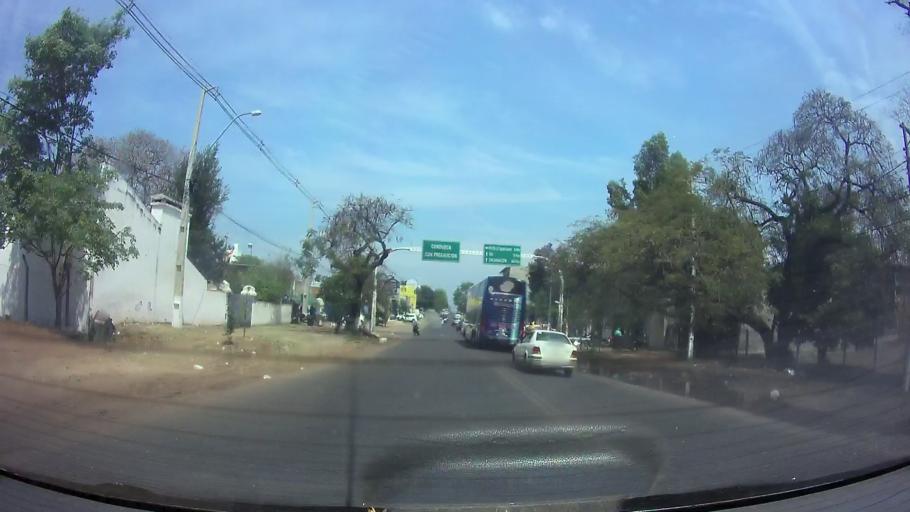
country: PY
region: Central
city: Capiata
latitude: -25.3722
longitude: -57.4786
